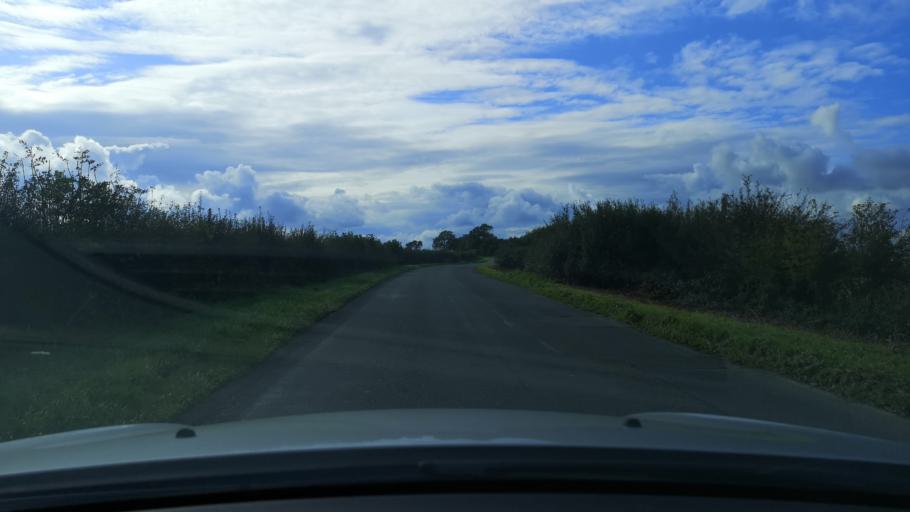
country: GB
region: England
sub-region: East Riding of Yorkshire
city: Walkington
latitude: 53.8261
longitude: -0.5175
